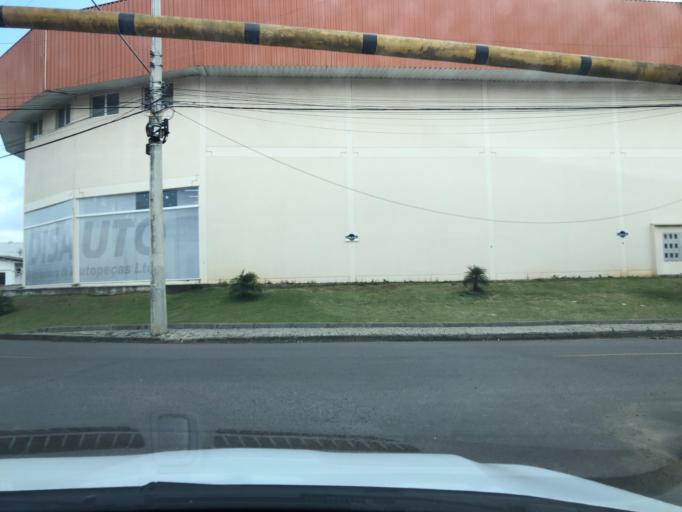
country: BR
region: Santa Catarina
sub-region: Rio Do Sul
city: Rio do Sul
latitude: -27.1918
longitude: -49.6248
